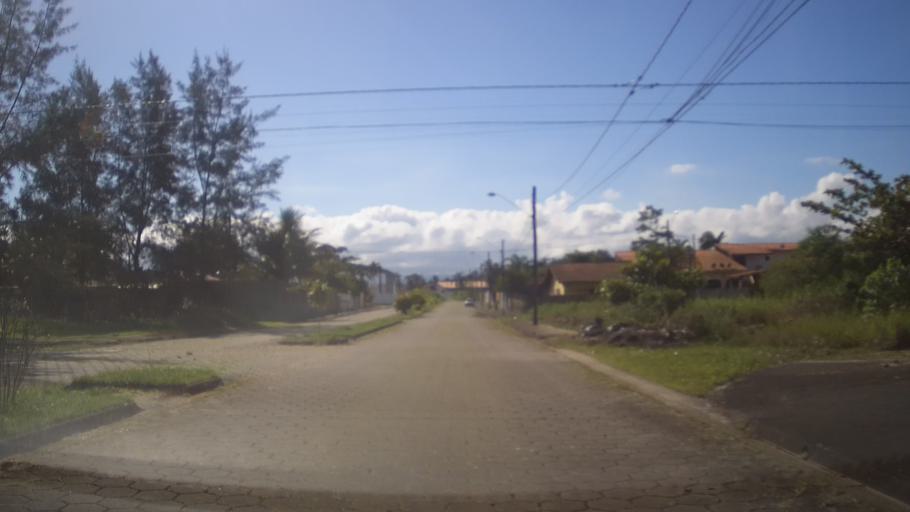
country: BR
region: Sao Paulo
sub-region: Itanhaem
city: Itanhaem
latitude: -24.2204
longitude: -46.8580
